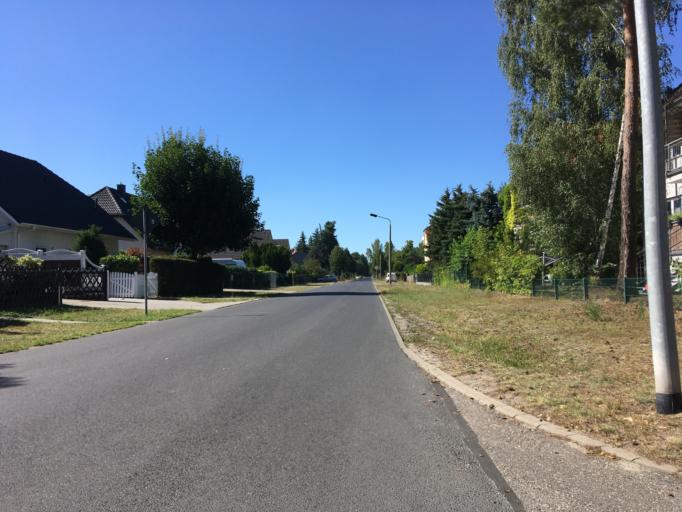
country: DE
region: Brandenburg
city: Zeuthen
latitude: 52.3473
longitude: 13.6007
